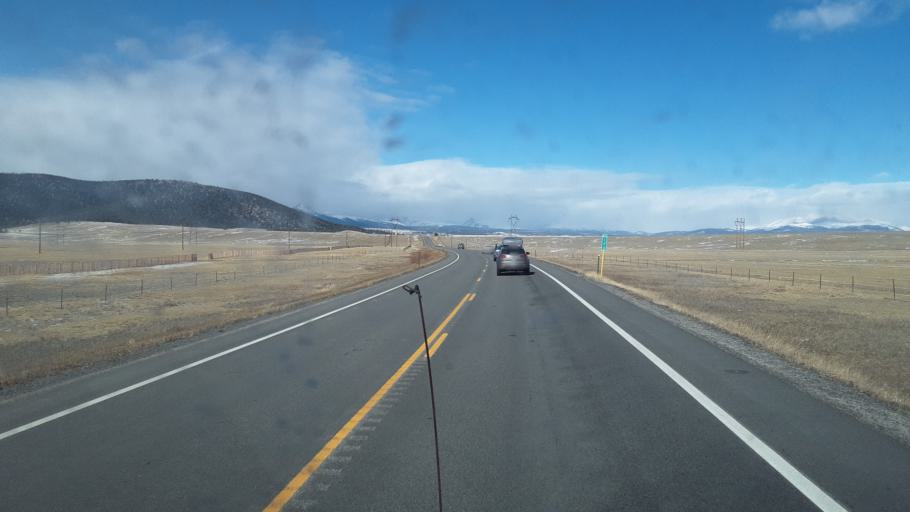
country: US
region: Colorado
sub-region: Park County
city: Fairplay
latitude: 39.0802
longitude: -105.9747
